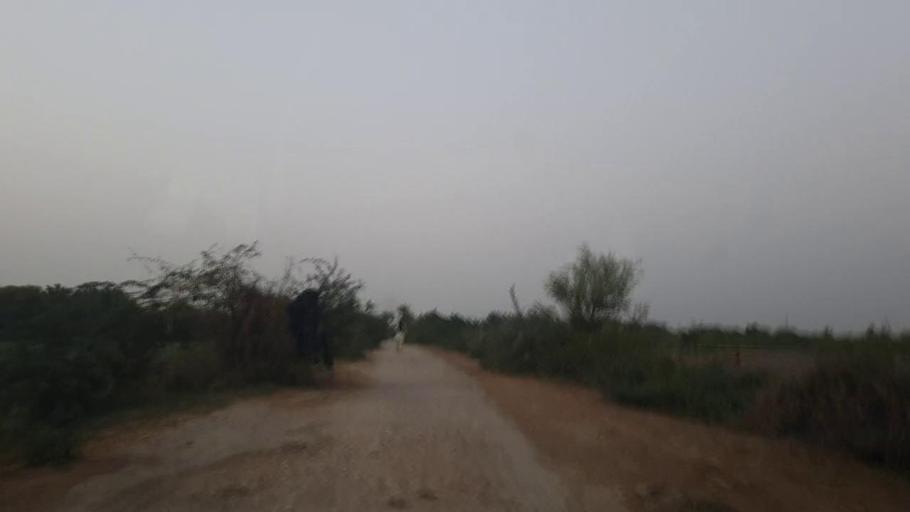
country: PK
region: Sindh
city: Mirpur Sakro
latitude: 24.5868
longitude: 67.7838
